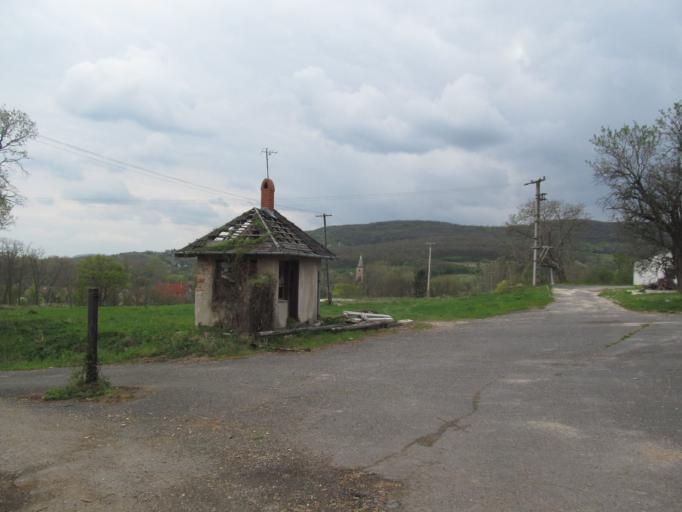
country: HU
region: Veszprem
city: Zanka
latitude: 46.9122
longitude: 17.6195
